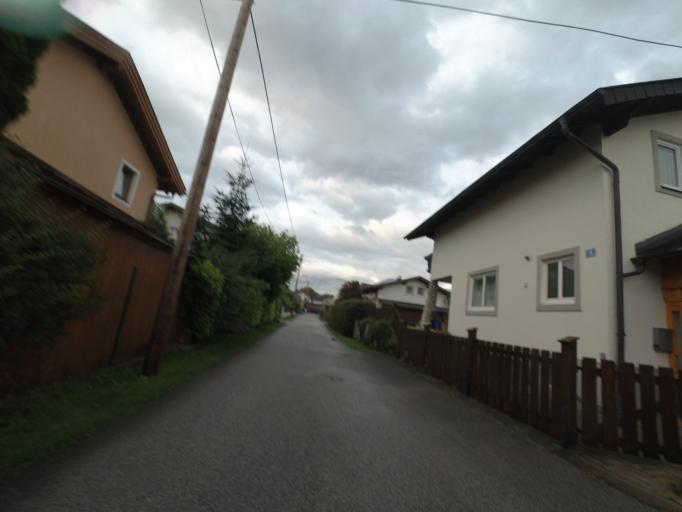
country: AT
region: Salzburg
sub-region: Politischer Bezirk Hallein
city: Puch bei Hallein
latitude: 47.7284
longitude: 13.0760
